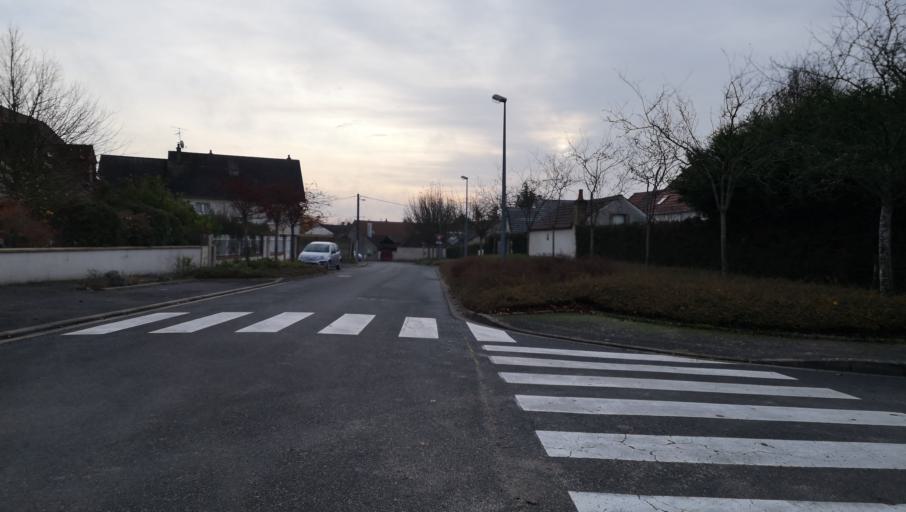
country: FR
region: Centre
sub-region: Departement du Loiret
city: Semoy
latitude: 47.9300
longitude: 1.9356
